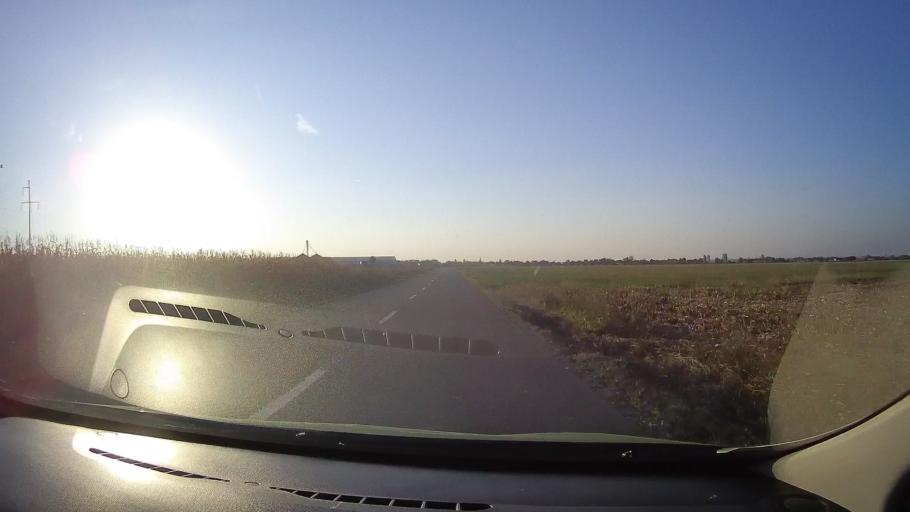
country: RO
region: Bihor
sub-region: Comuna Biharea
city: Biharea
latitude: 47.1625
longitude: 21.9601
